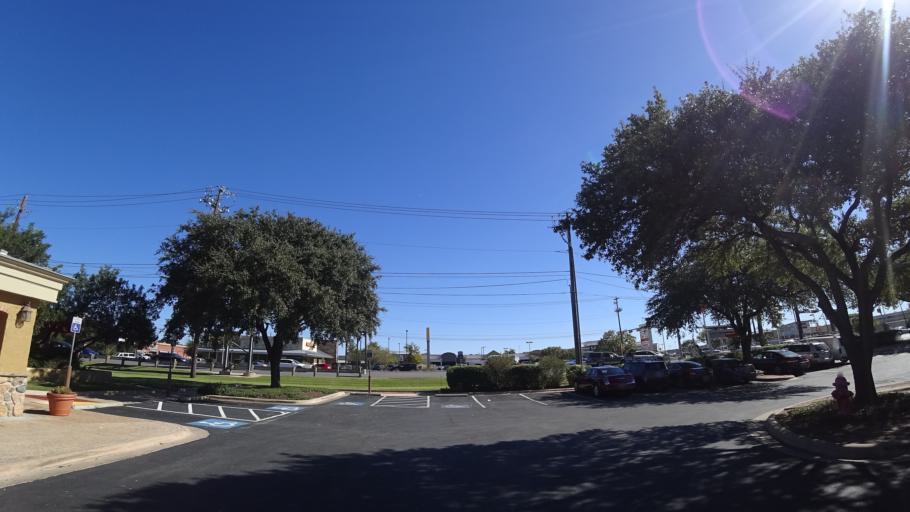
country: US
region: Texas
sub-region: Travis County
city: Rollingwood
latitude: 30.2369
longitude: -97.7924
